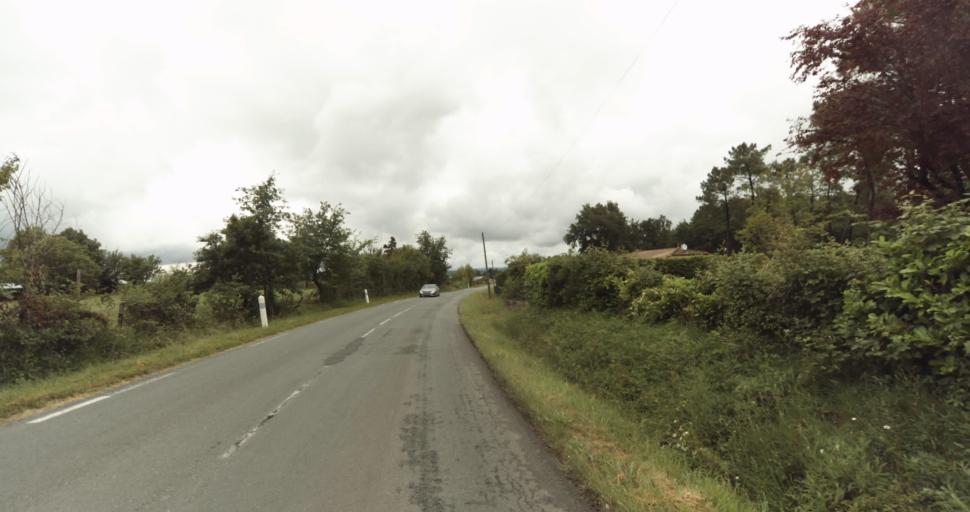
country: FR
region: Aquitaine
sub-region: Departement de la Dordogne
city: Beaumont-du-Perigord
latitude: 44.7507
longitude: 0.7746
